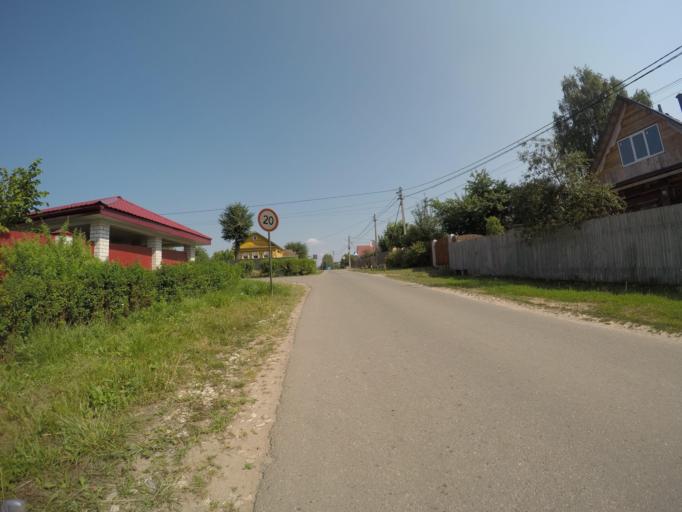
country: RU
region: Moskovskaya
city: Rechitsy
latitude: 55.6352
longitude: 38.5075
